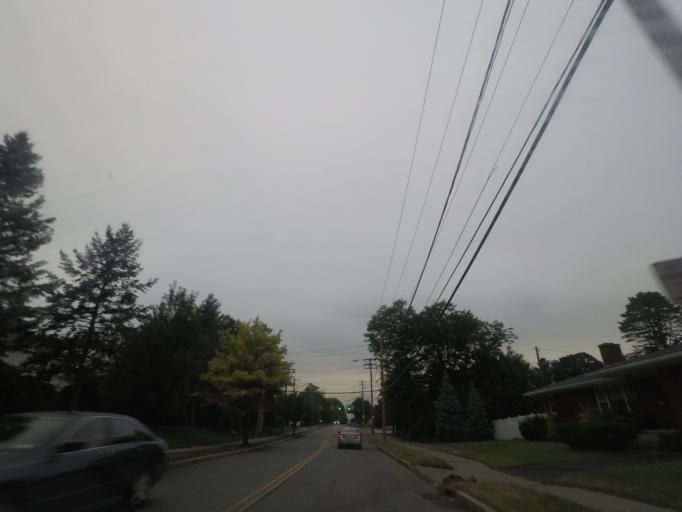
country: US
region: New York
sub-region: Albany County
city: Delmar
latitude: 42.6484
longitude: -73.8041
